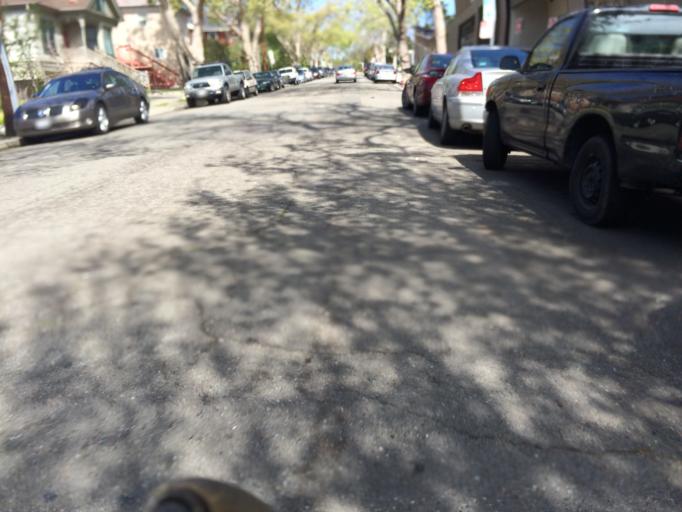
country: US
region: California
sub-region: Alameda County
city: Berkeley
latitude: 37.8803
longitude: -122.2705
